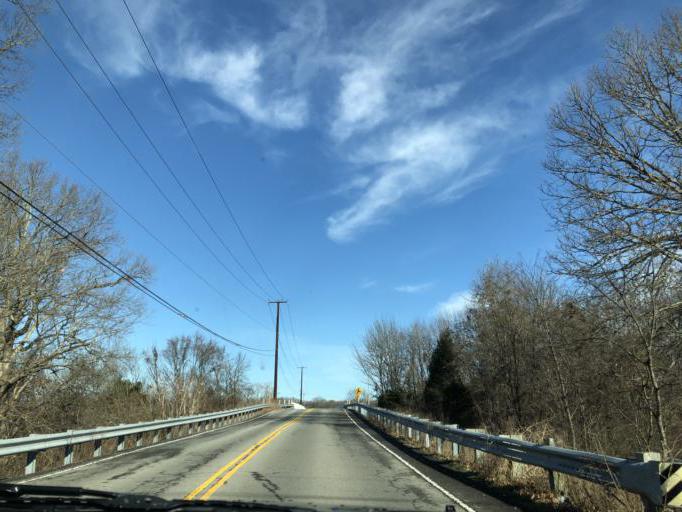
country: US
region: Tennessee
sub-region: Wilson County
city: Green Hill
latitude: 36.1685
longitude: -86.5855
